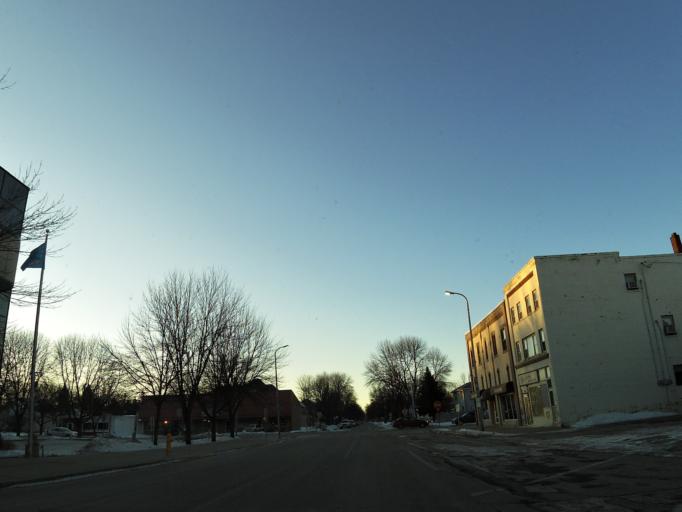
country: US
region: North Dakota
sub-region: Grand Forks County
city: Grand Forks
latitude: 47.9262
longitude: -97.0344
